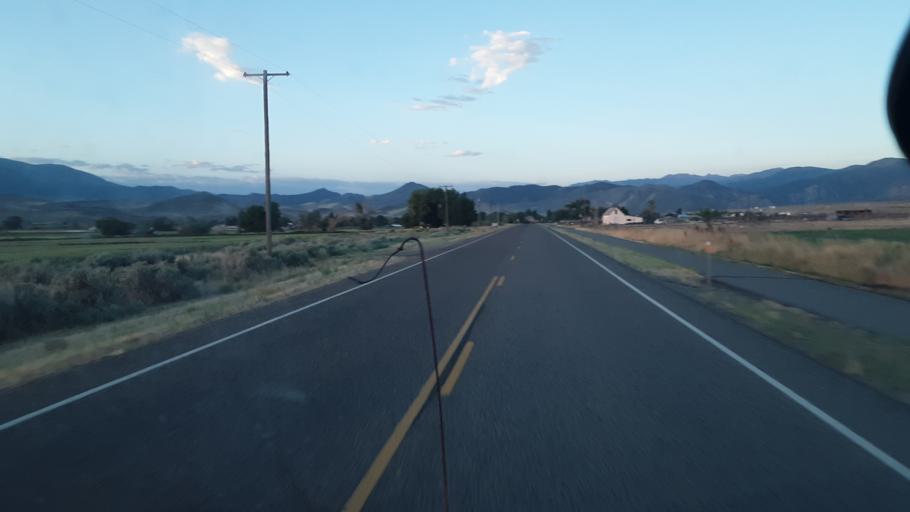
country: US
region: Utah
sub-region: Sevier County
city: Monroe
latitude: 38.6375
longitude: -112.2168
